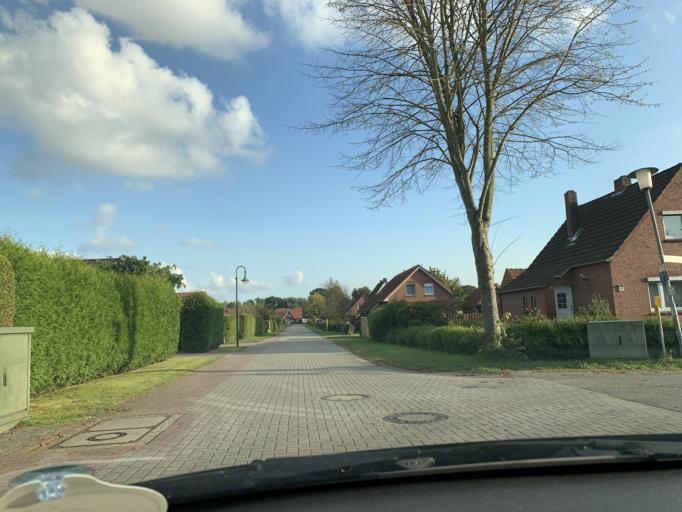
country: DE
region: Lower Saxony
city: Apen
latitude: 53.2431
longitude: 7.7854
